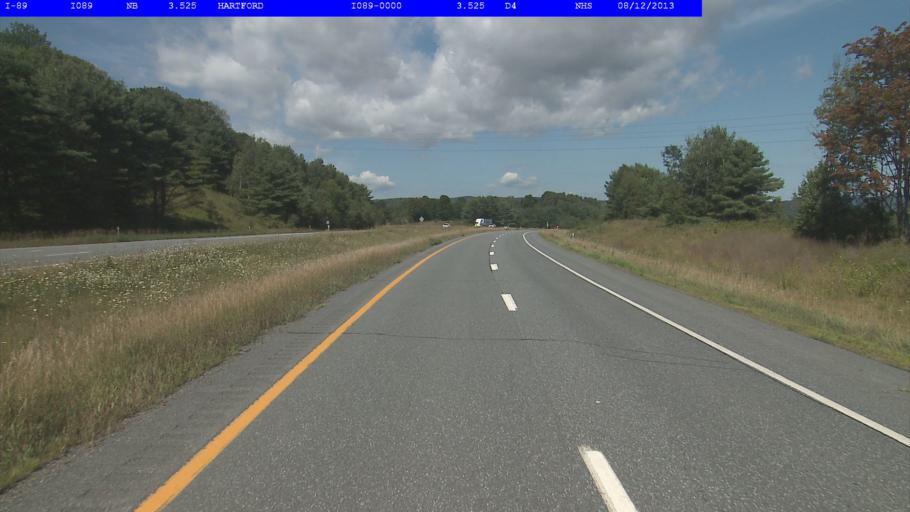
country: US
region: Vermont
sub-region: Windsor County
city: White River Junction
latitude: 43.6636
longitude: -72.3789
